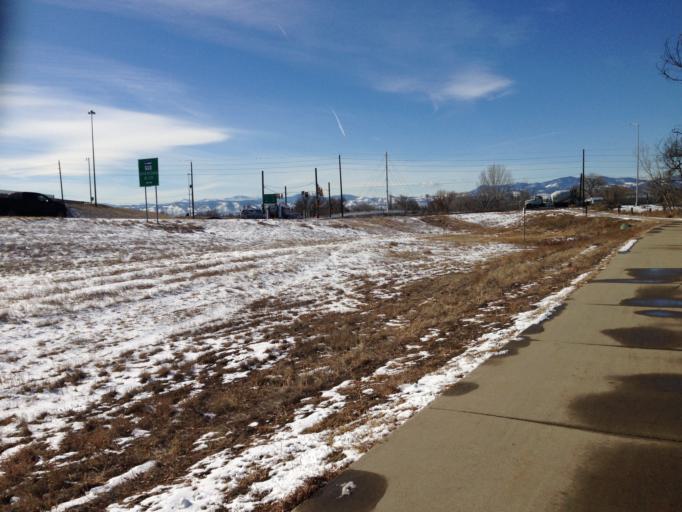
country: US
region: Colorado
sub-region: Adams County
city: Berkley
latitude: 39.7976
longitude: -105.0517
